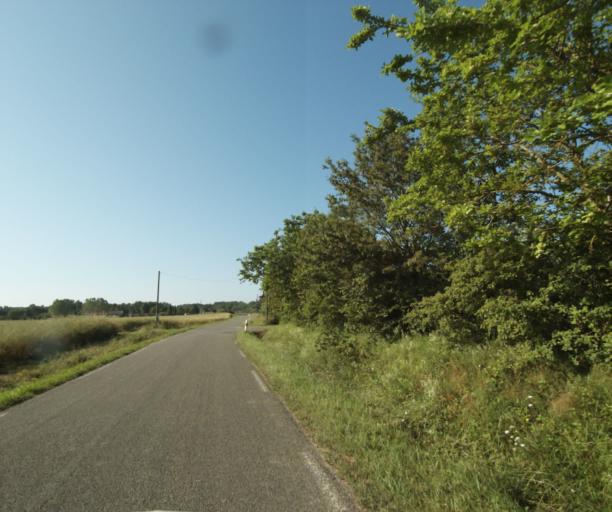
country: FR
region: Midi-Pyrenees
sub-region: Departement du Tarn-et-Garonne
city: Saint-Etienne-de-Tulmont
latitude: 44.0284
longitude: 1.4260
